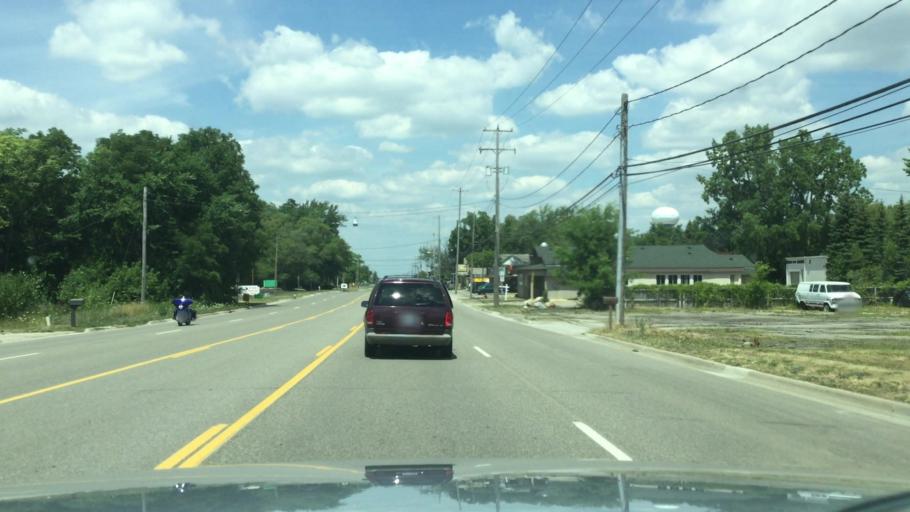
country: US
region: Michigan
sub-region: Genesee County
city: Grand Blanc
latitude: 42.9476
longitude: -83.6540
